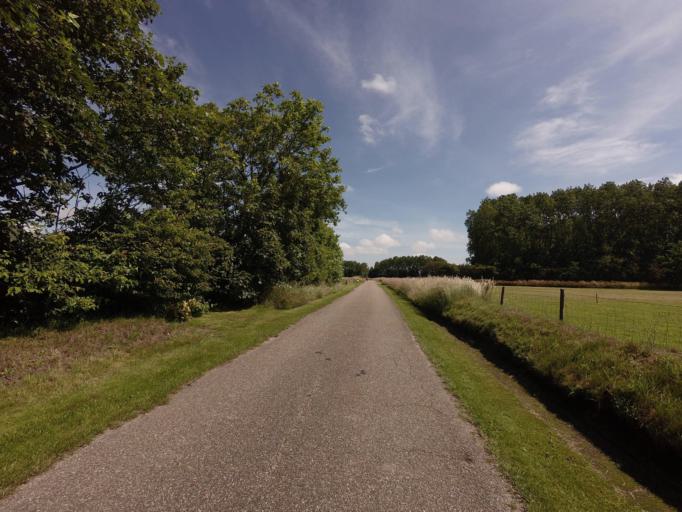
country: NL
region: North Holland
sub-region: Gemeente Texel
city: Den Burg
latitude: 53.0676
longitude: 4.8131
